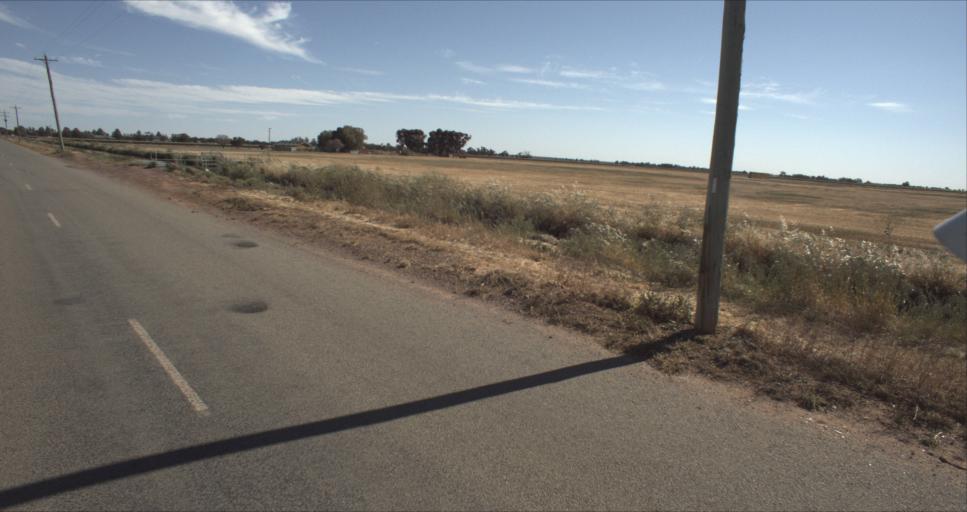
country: AU
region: New South Wales
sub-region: Leeton
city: Leeton
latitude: -34.5748
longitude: 146.3810
